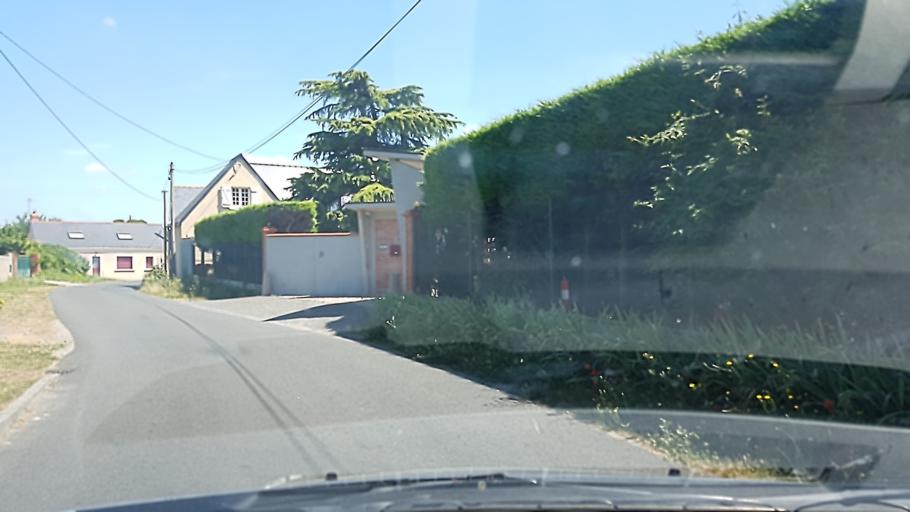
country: FR
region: Pays de la Loire
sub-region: Departement de Maine-et-Loire
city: Le Plessis-Grammoire
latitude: 47.5108
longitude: -0.4101
